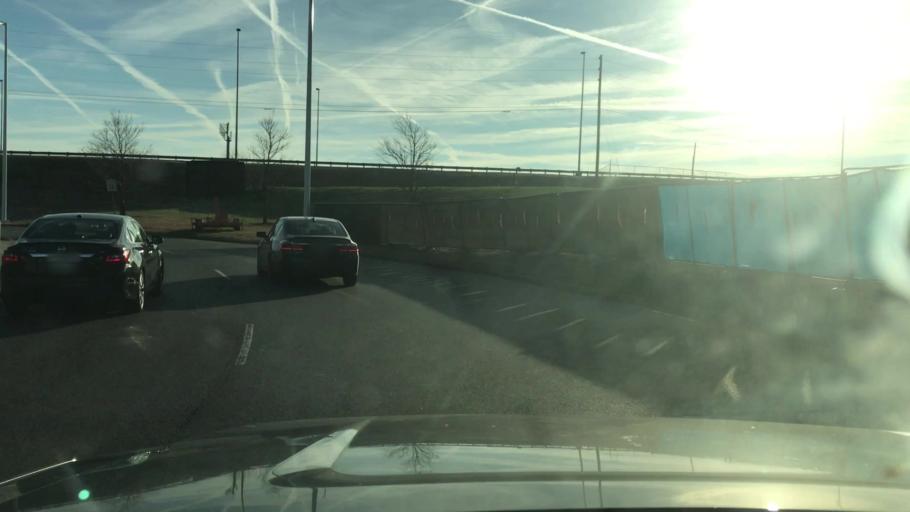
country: US
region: Tennessee
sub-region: Davidson County
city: Lakewood
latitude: 36.1298
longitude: -86.6666
